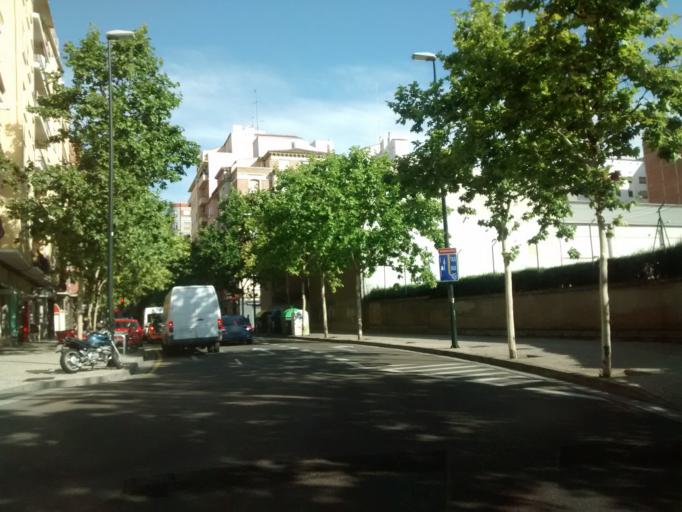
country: ES
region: Aragon
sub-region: Provincia de Zaragoza
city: Delicias
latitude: 41.6423
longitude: -0.8915
